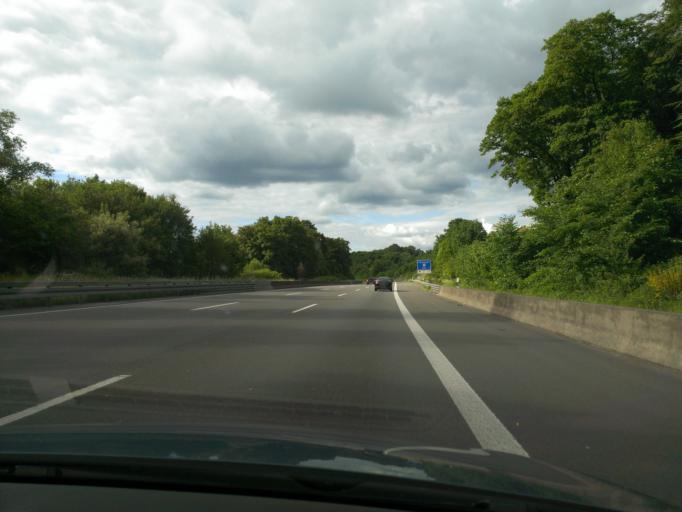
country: DE
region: North Rhine-Westphalia
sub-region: Regierungsbezirk Dusseldorf
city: Remscheid
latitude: 51.2334
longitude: 7.2308
